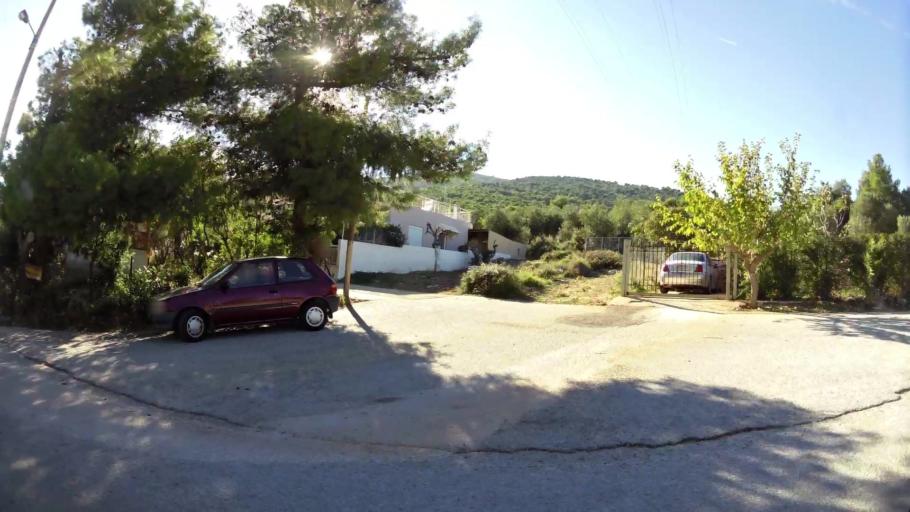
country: GR
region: Attica
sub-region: Nomarchia Anatolikis Attikis
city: Leondarion
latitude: 37.9938
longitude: 23.8425
